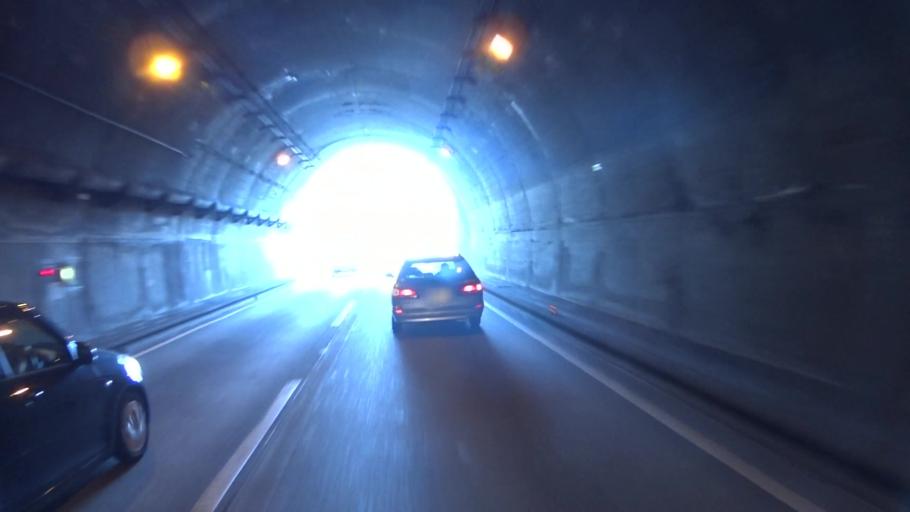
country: JP
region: Shiga Prefecture
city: Otsu-shi
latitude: 35.0319
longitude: 135.8506
